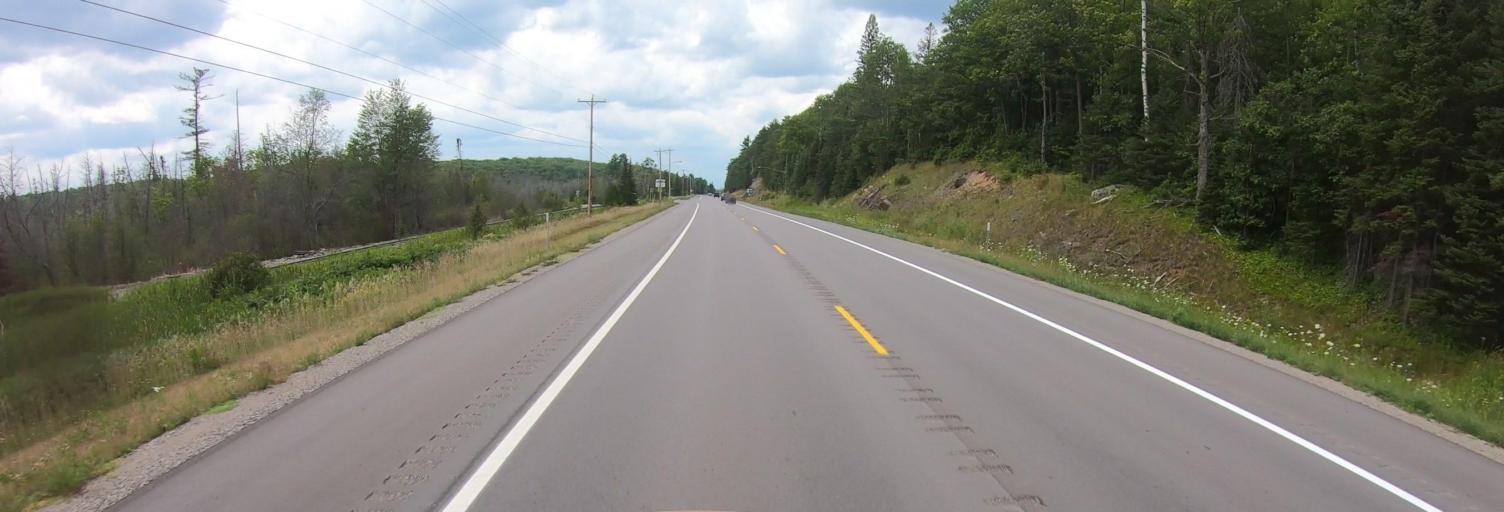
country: US
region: Michigan
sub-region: Baraga County
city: L'Anse
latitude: 46.5444
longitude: -88.1617
